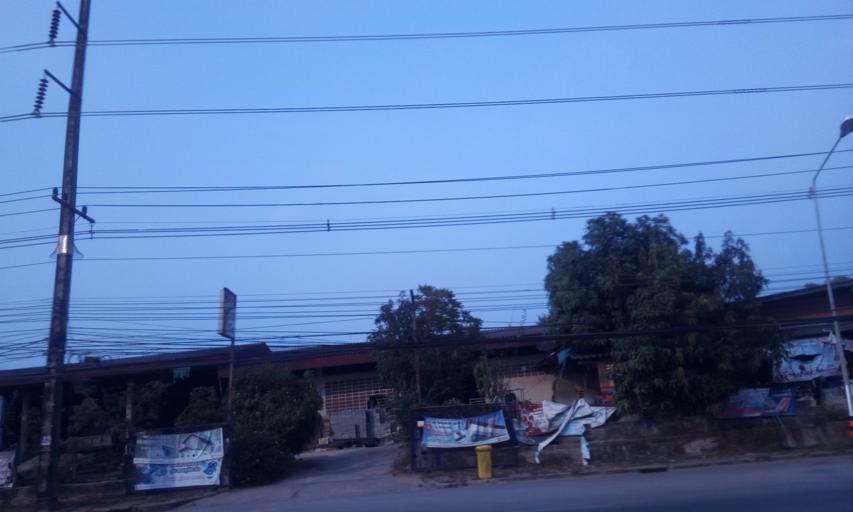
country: TH
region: Trat
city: Khao Saming
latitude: 12.3750
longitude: 102.3830
